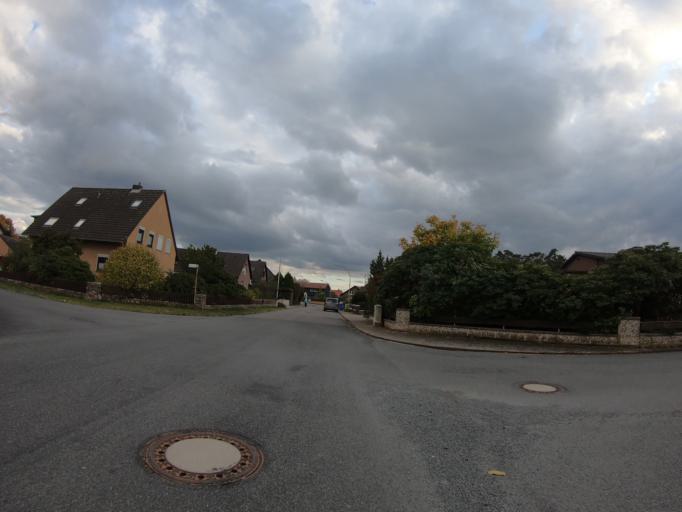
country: DE
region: Lower Saxony
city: Wagenhoff
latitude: 52.5279
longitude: 10.5254
